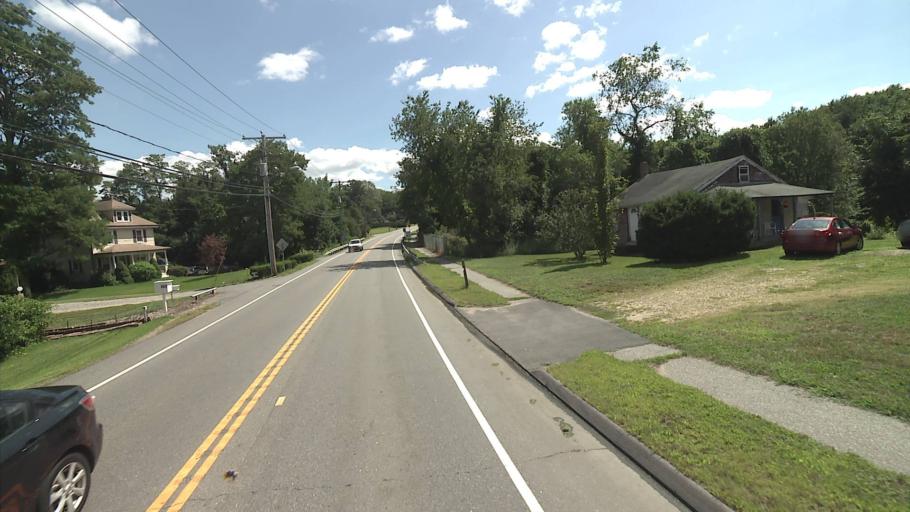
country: US
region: Connecticut
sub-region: New London County
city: Niantic
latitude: 41.3689
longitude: -72.1898
